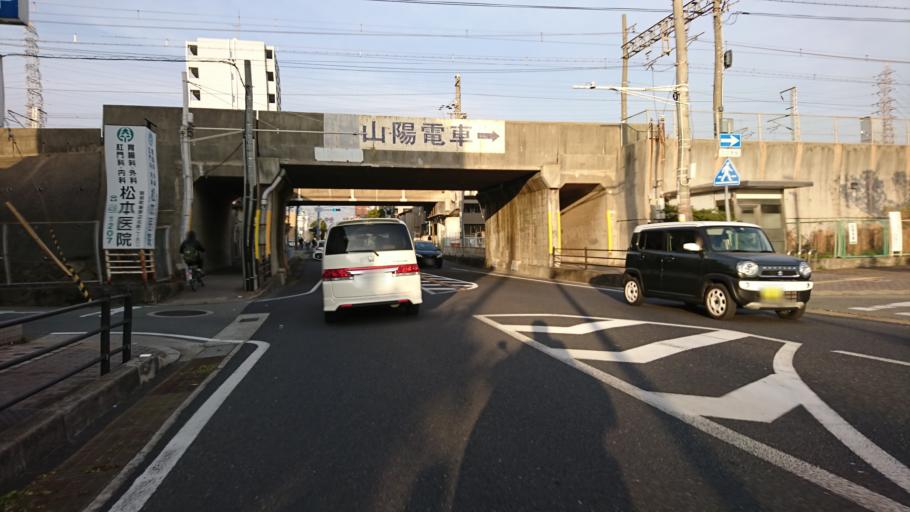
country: JP
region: Hyogo
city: Kakogawacho-honmachi
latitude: 34.7303
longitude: 134.8499
